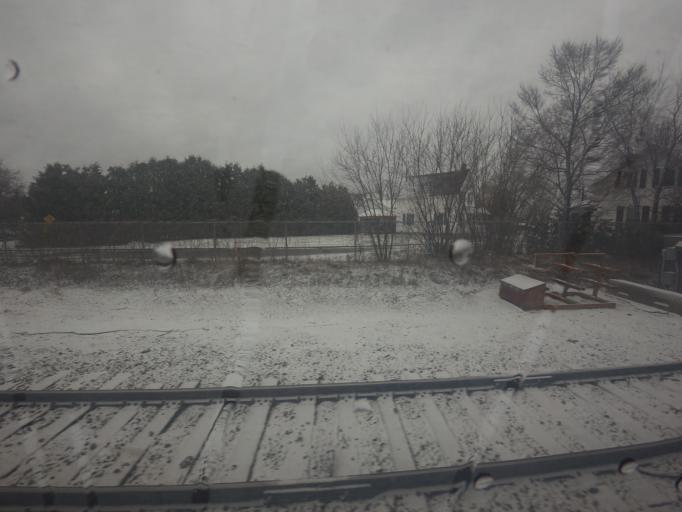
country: CA
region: Ontario
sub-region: Lanark County
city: Smiths Falls
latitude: 44.9081
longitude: -76.0204
